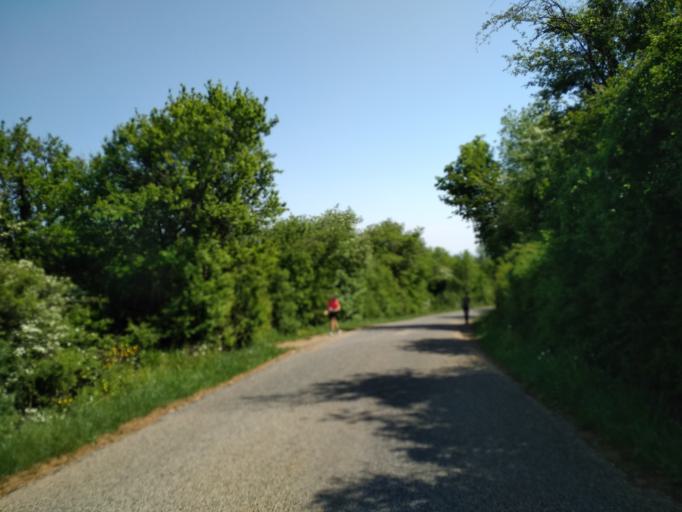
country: FR
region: Rhone-Alpes
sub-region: Departement du Rhone
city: Limonest
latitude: 45.8410
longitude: 4.8006
